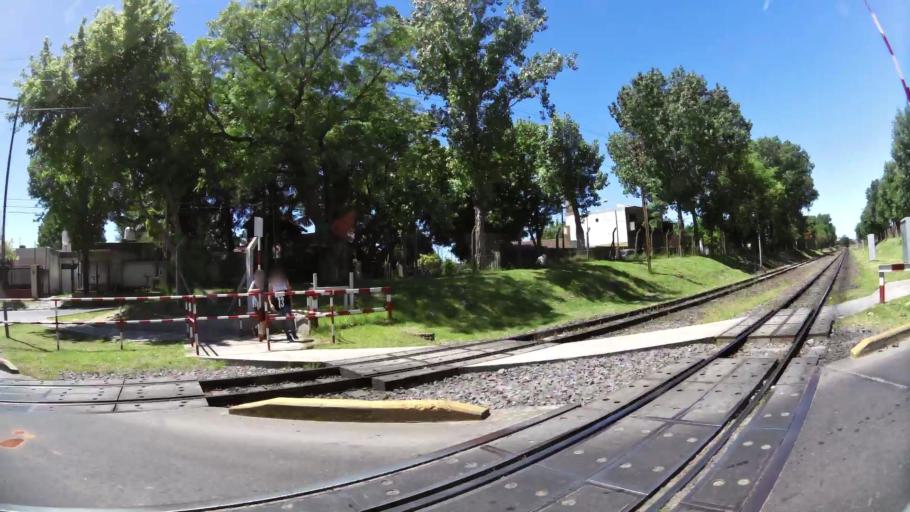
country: AR
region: Buenos Aires
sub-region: Partido de San Isidro
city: San Isidro
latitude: -34.5072
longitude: -58.5741
